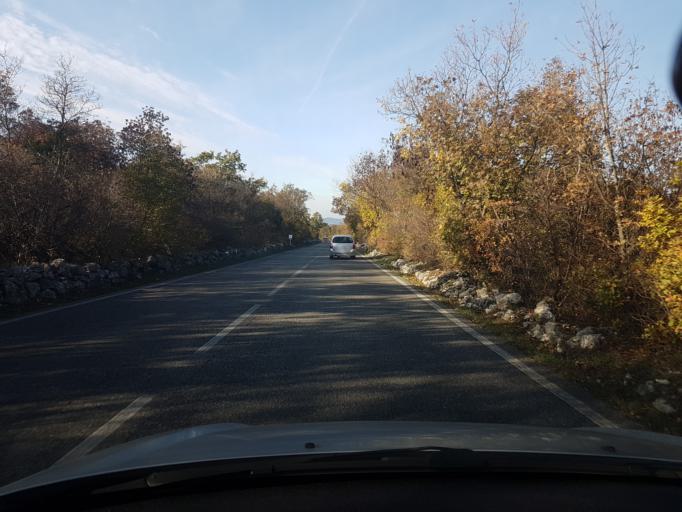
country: IT
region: Friuli Venezia Giulia
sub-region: Provincia di Trieste
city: Santa Croce
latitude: 45.7247
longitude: 13.7143
